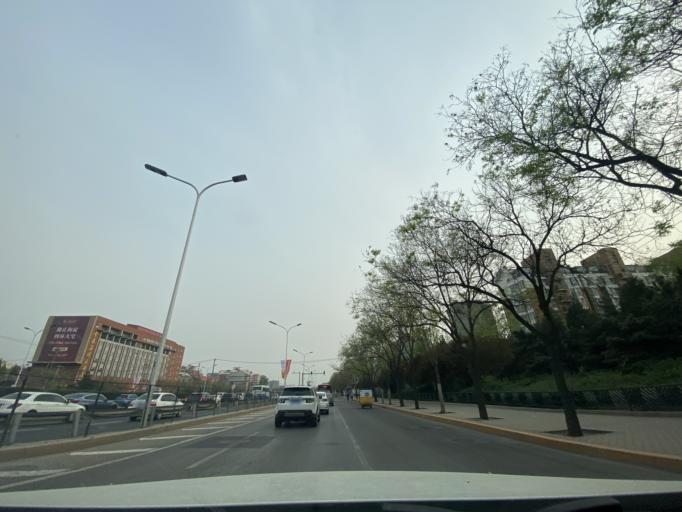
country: CN
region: Beijing
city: Sijiqing
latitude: 39.9381
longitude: 116.2679
